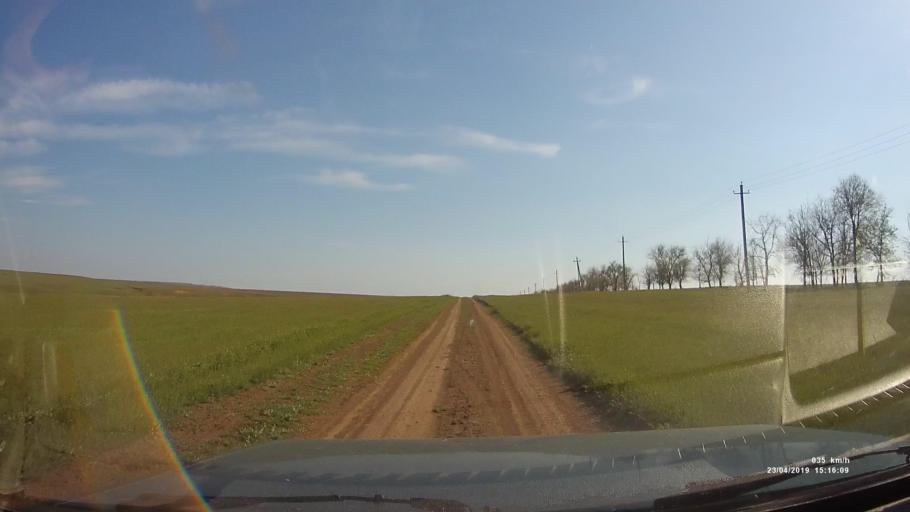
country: RU
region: Rostov
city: Remontnoye
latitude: 46.5353
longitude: 42.9697
